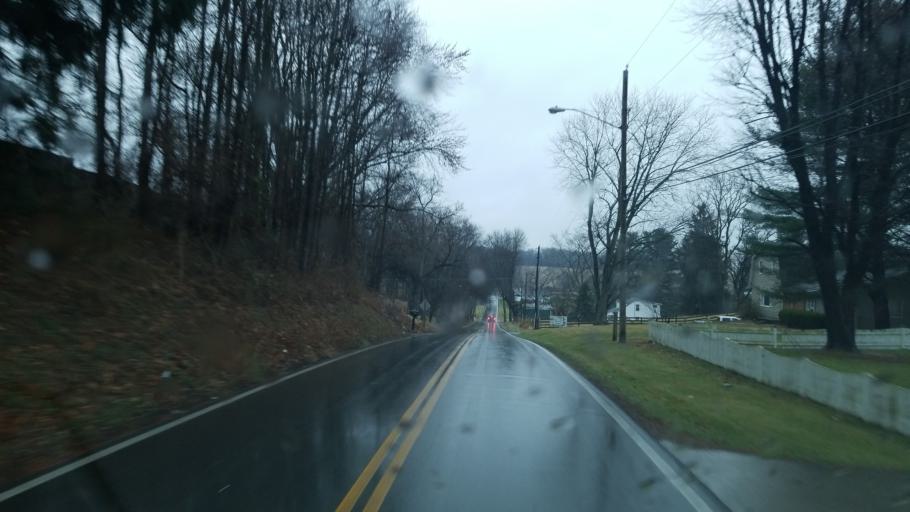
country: US
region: Ohio
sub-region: Licking County
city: Newark
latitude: 40.0811
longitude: -82.3885
